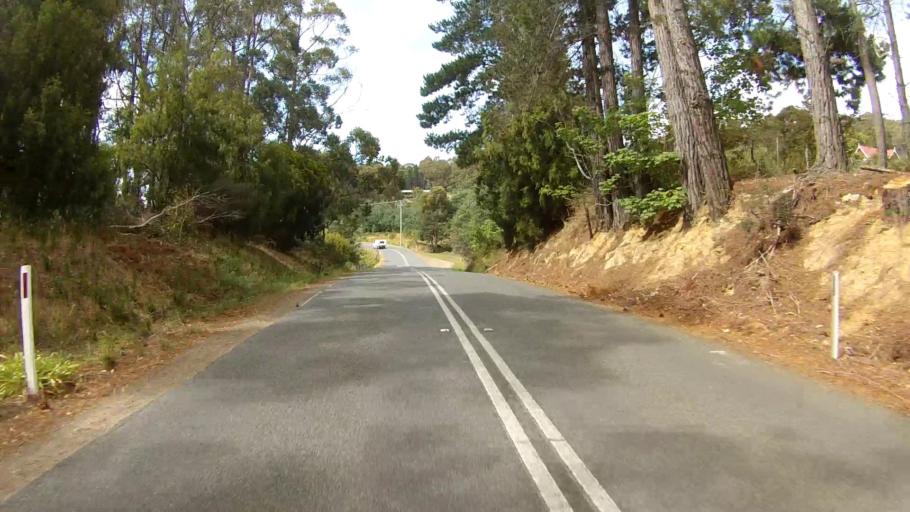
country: AU
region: Tasmania
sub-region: Kingborough
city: Kettering
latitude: -43.1897
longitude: 147.2454
